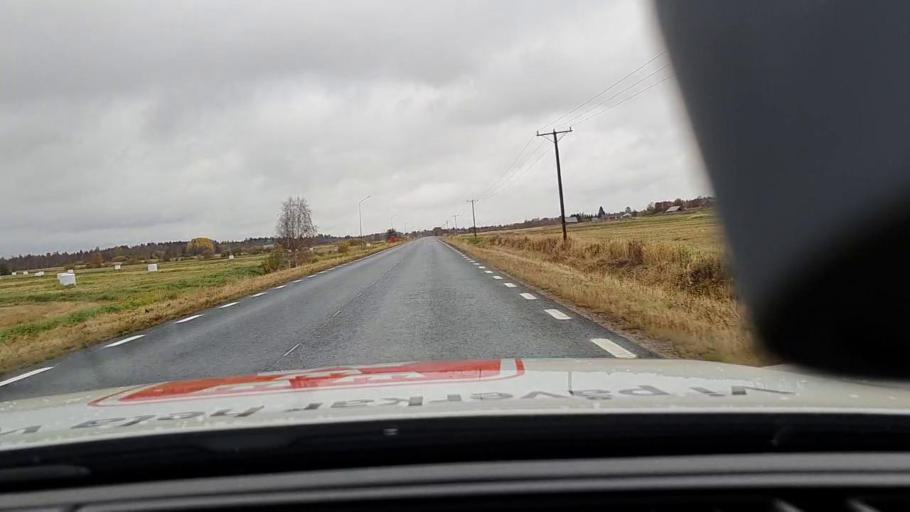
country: FI
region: Lapland
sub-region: Kemi-Tornio
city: Tornio
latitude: 65.9835
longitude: 24.0259
